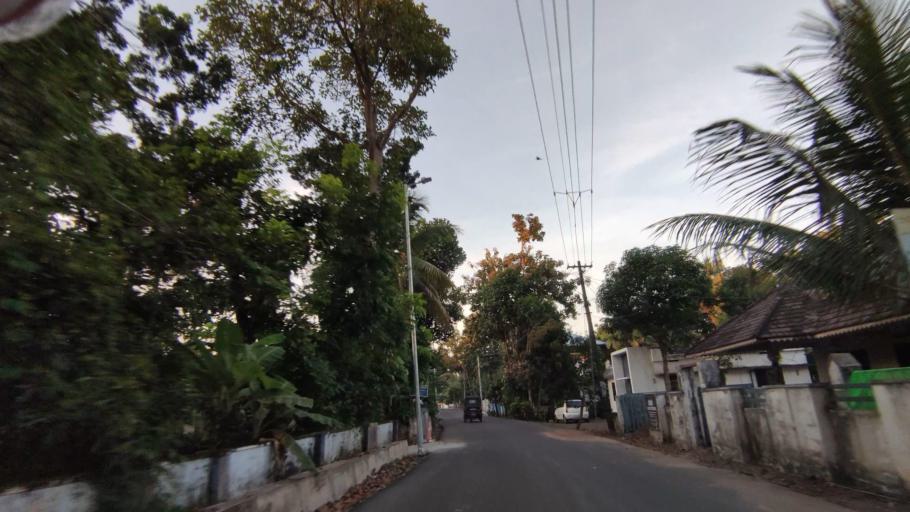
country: IN
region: Kerala
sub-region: Kottayam
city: Kottayam
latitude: 9.6378
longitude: 76.4963
